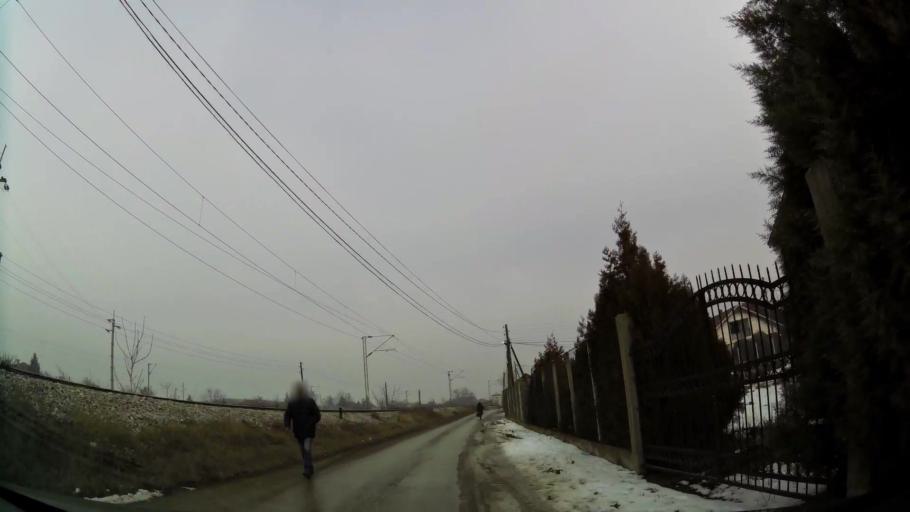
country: MK
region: Ilinden
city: Ilinden
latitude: 41.9972
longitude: 21.5617
